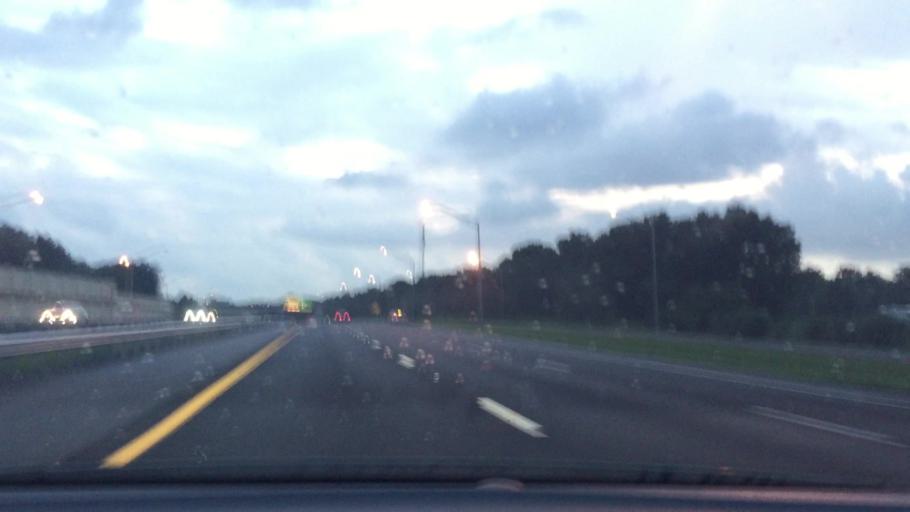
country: US
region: Florida
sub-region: Orange County
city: Orlovista
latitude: 28.5494
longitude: -81.4783
